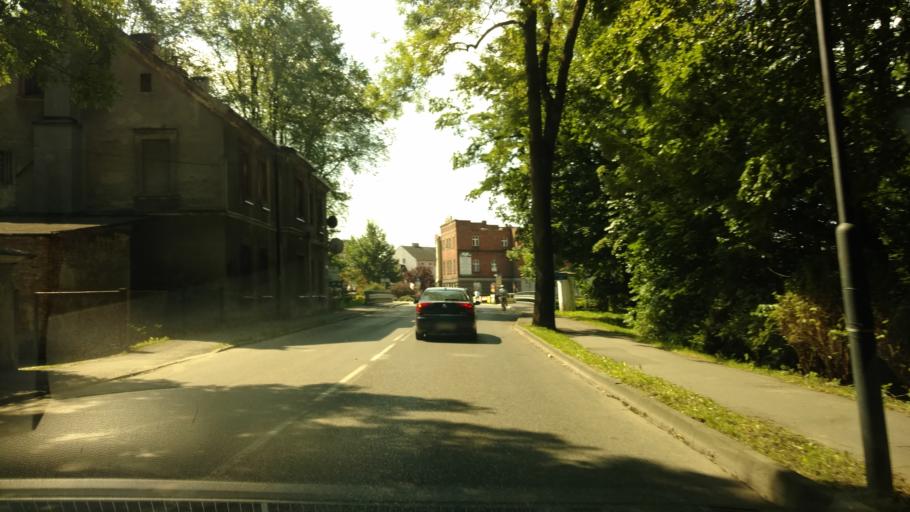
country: PL
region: Silesian Voivodeship
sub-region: Powiat pszczynski
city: Pszczyna
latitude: 49.9800
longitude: 18.9457
